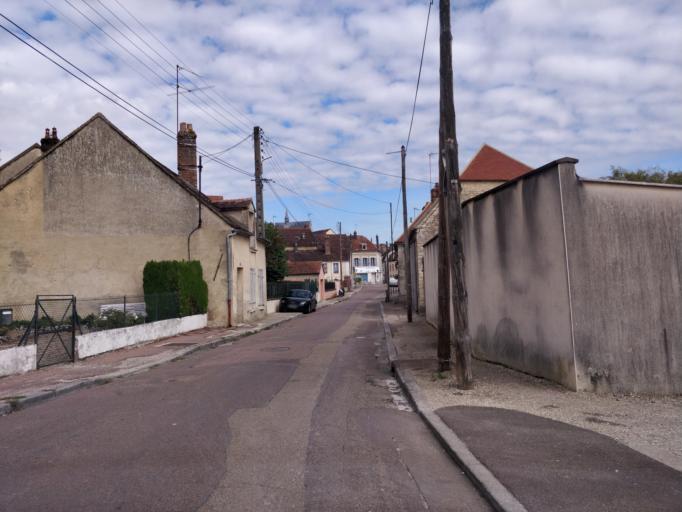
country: FR
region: Bourgogne
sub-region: Departement de l'Yonne
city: Saint-Florentin
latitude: 47.9986
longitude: 3.7257
